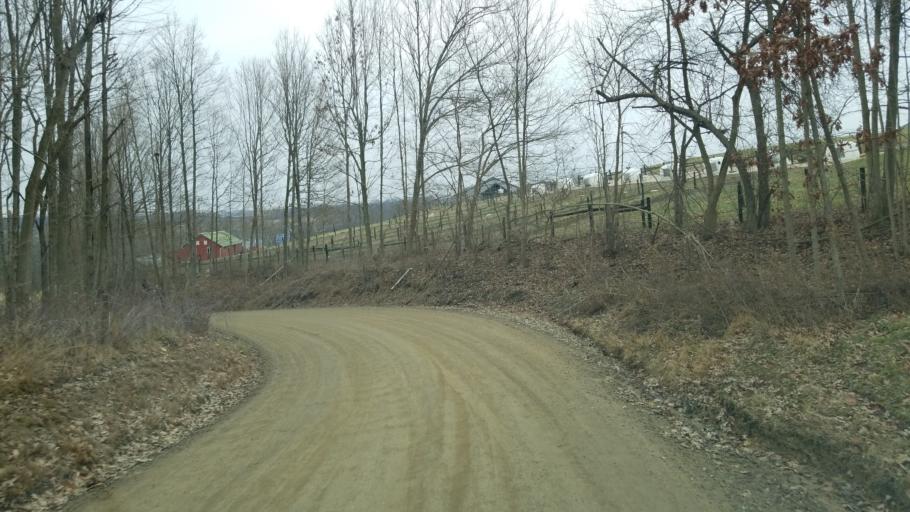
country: US
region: Ohio
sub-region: Holmes County
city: Millersburg
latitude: 40.4404
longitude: -81.8372
